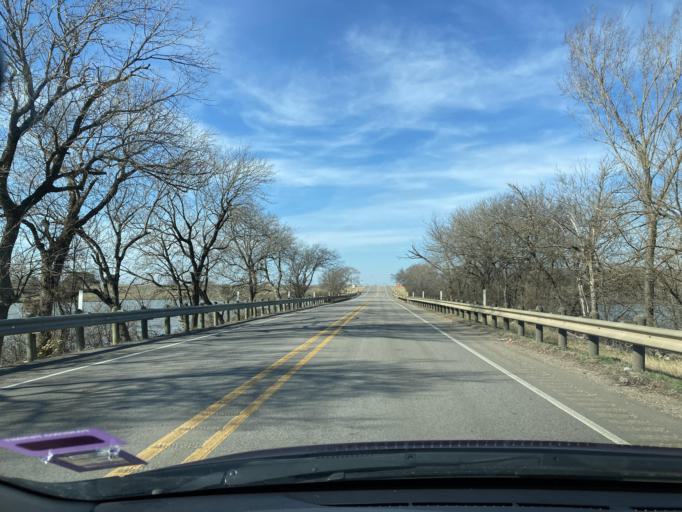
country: US
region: Texas
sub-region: Navarro County
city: Corsicana
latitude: 32.0535
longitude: -96.4246
